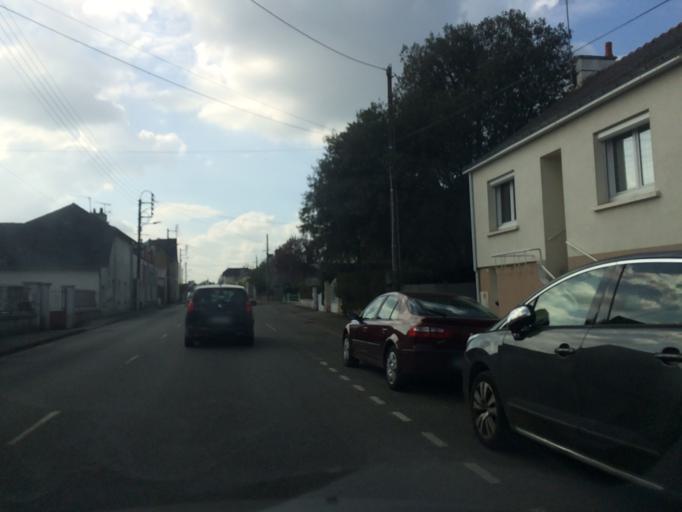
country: FR
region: Pays de la Loire
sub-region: Departement de la Loire-Atlantique
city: Blain
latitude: 47.4773
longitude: -1.7682
